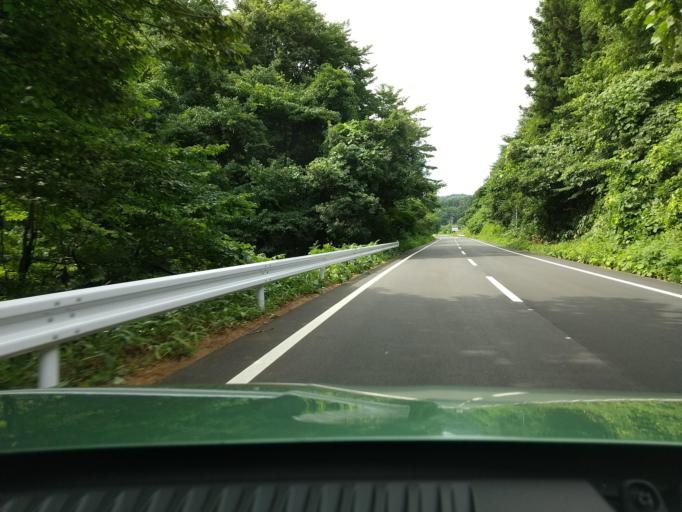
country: JP
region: Akita
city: Akita
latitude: 39.7185
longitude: 140.1892
